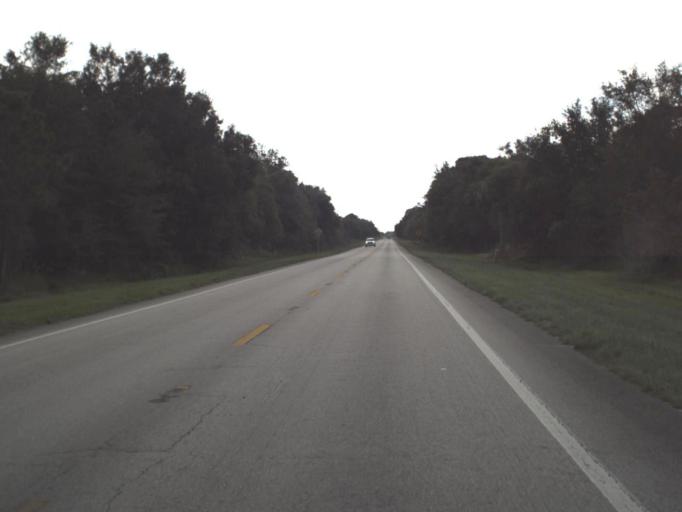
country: US
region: Florida
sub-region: Okeechobee County
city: Cypress Quarters
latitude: 27.3684
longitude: -80.8185
